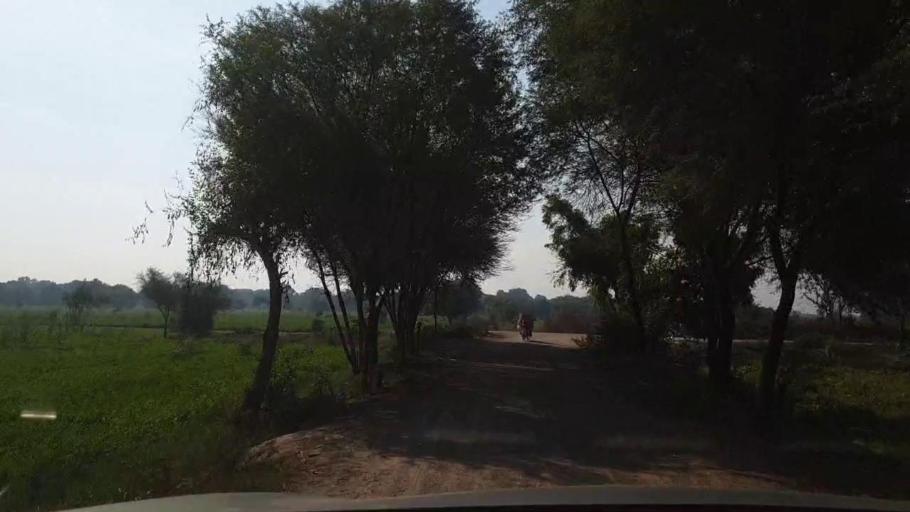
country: PK
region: Sindh
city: Tando Allahyar
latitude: 25.5898
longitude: 68.7382
